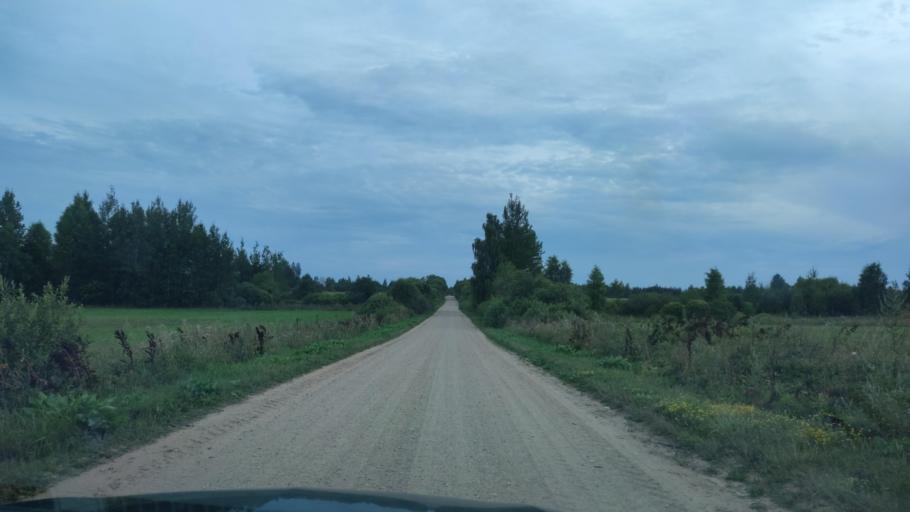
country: BY
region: Vitebsk
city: Mosar
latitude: 55.1249
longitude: 27.1564
